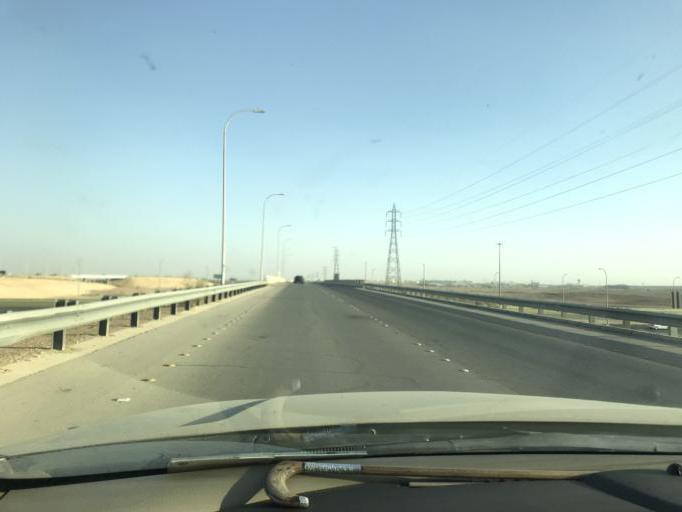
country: SA
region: Ar Riyad
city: Riyadh
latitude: 24.9036
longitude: 46.7050
